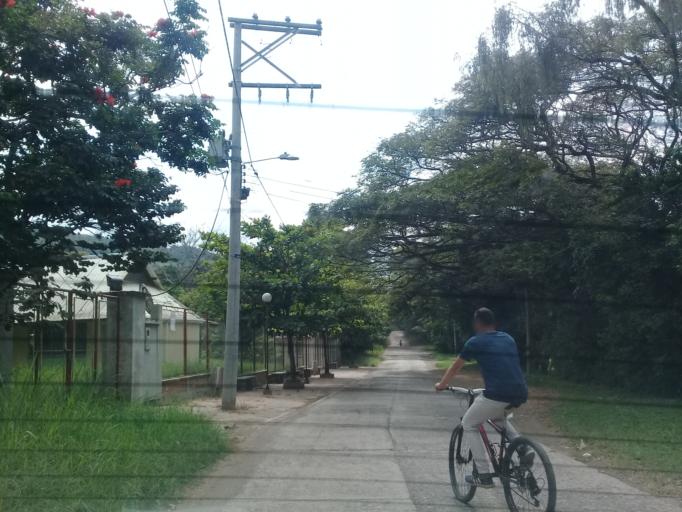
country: CO
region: Cundinamarca
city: Guaduas
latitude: 5.0602
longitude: -74.5986
